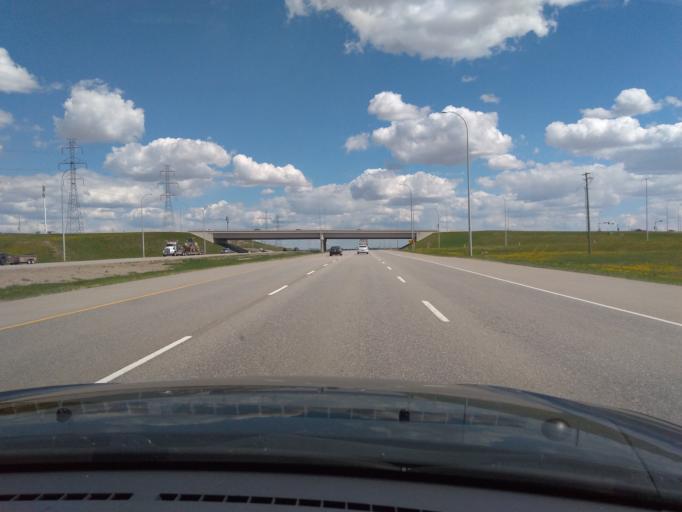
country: CA
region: Alberta
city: Calgary
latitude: 51.1735
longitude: -114.0731
